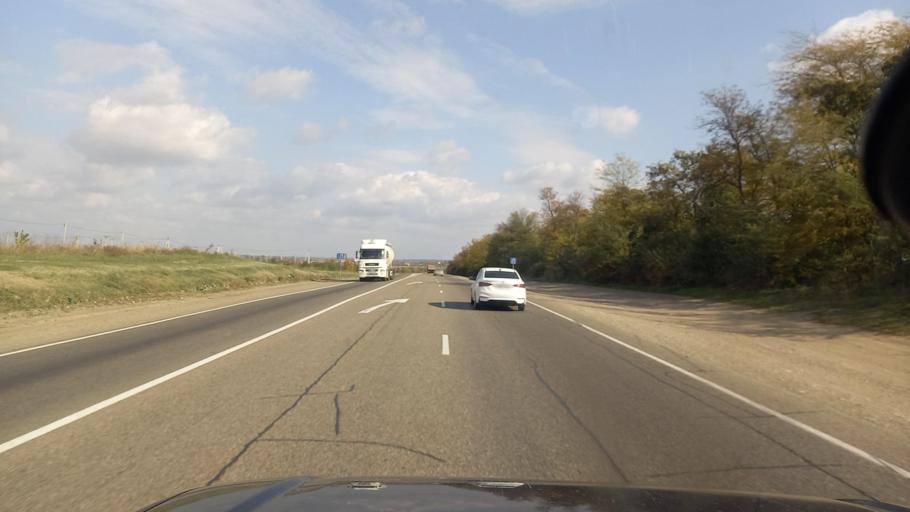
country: RU
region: Krasnodarskiy
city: Akhtyrskiy
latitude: 44.8479
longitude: 38.3140
